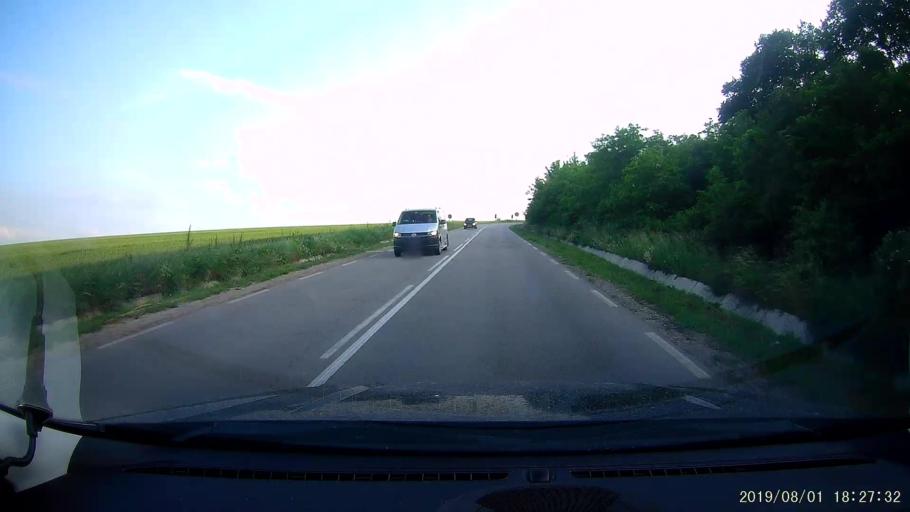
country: BG
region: Shumen
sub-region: Obshtina Venets
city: Venets
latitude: 43.5850
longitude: 26.9812
